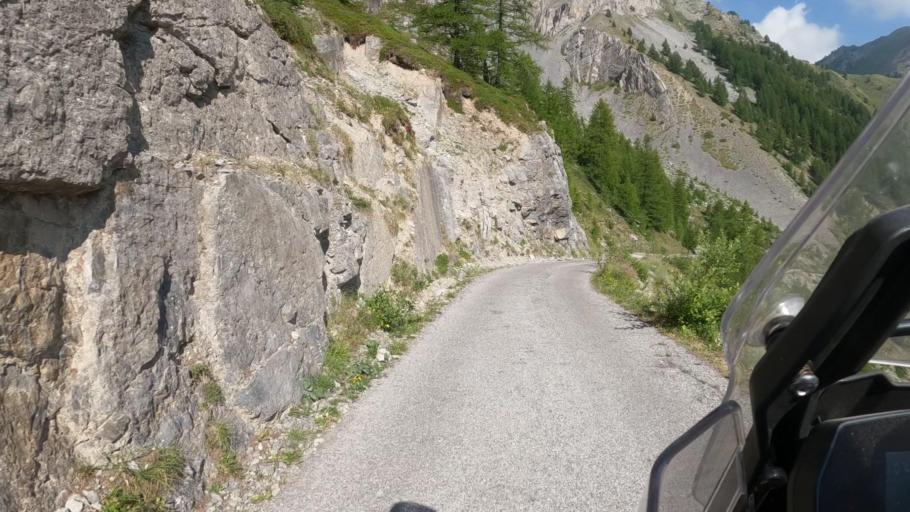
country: IT
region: Piedmont
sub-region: Provincia di Cuneo
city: Canosio
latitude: 44.4094
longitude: 7.0362
